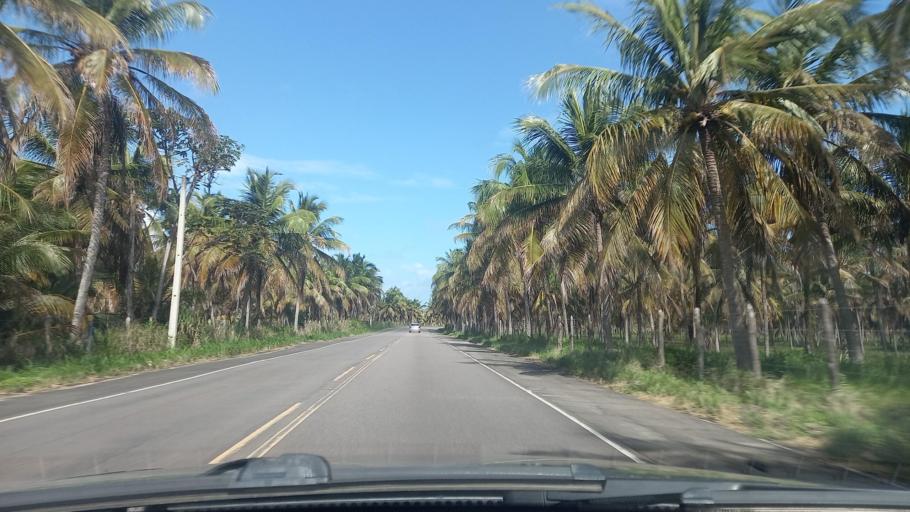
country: BR
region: Alagoas
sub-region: Marechal Deodoro
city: Marechal Deodoro
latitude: -9.8460
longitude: -35.9187
